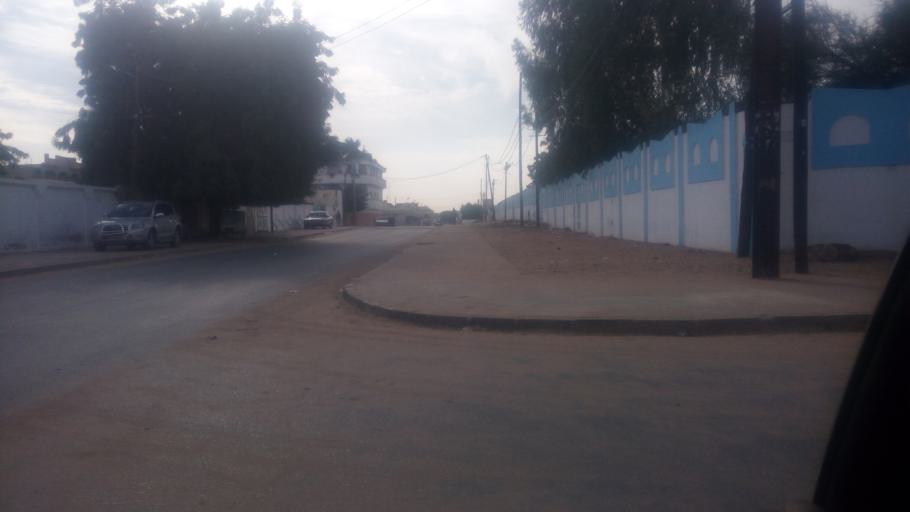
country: SN
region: Diourbel
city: Touba
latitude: 14.8643
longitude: -15.8828
